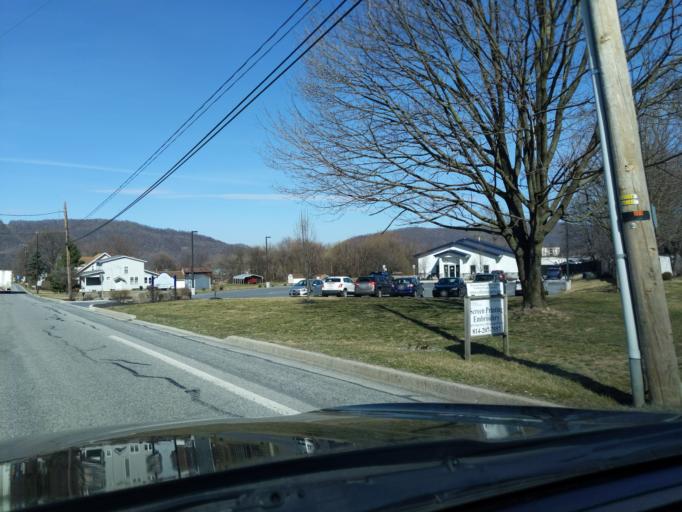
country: US
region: Pennsylvania
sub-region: Blair County
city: Roaring Spring
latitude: 40.3348
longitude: -78.3864
